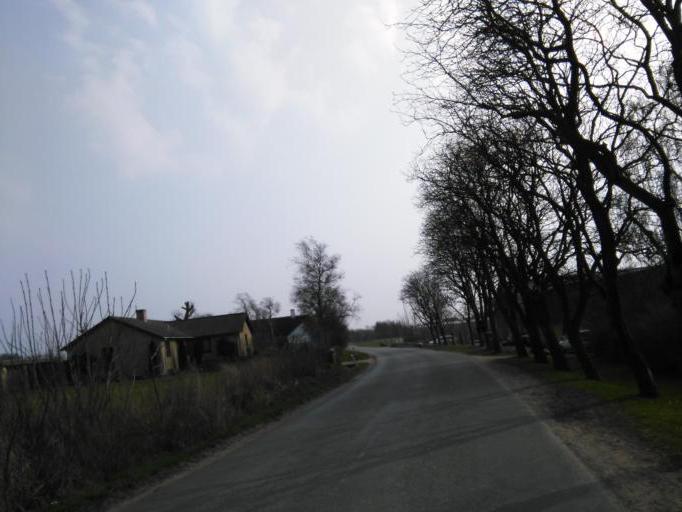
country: DK
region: Central Jutland
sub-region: Arhus Kommune
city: Beder
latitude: 56.0581
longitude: 10.2422
